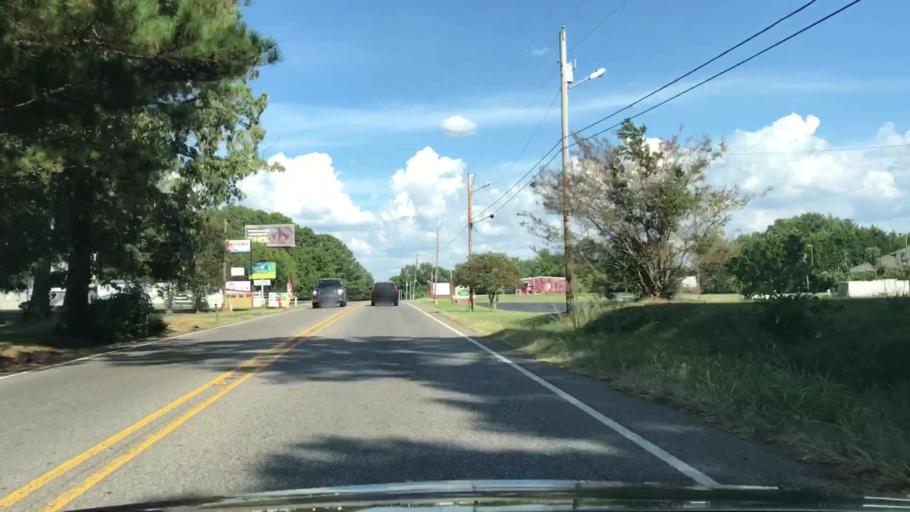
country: US
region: Tennessee
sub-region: Giles County
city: Ardmore
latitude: 34.9919
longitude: -86.8357
